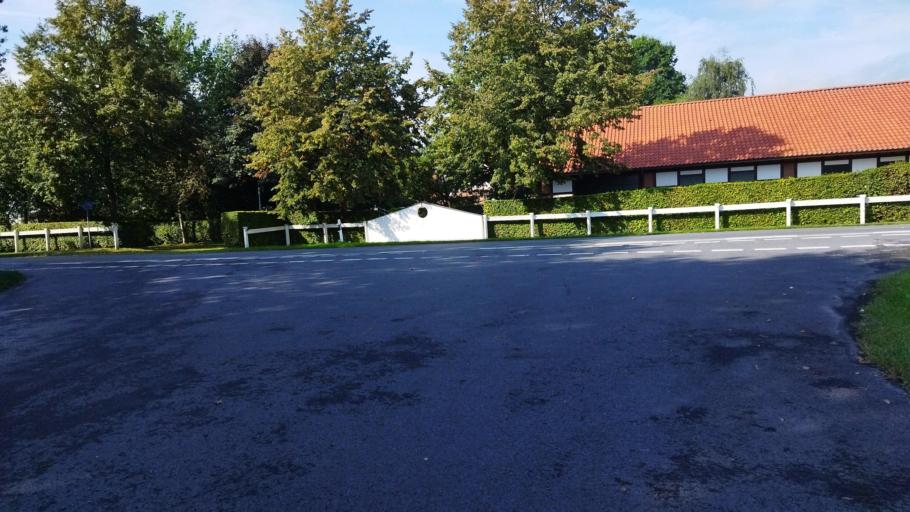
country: DE
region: North Rhine-Westphalia
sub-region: Regierungsbezirk Munster
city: Warendorf
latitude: 51.9764
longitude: 7.9946
